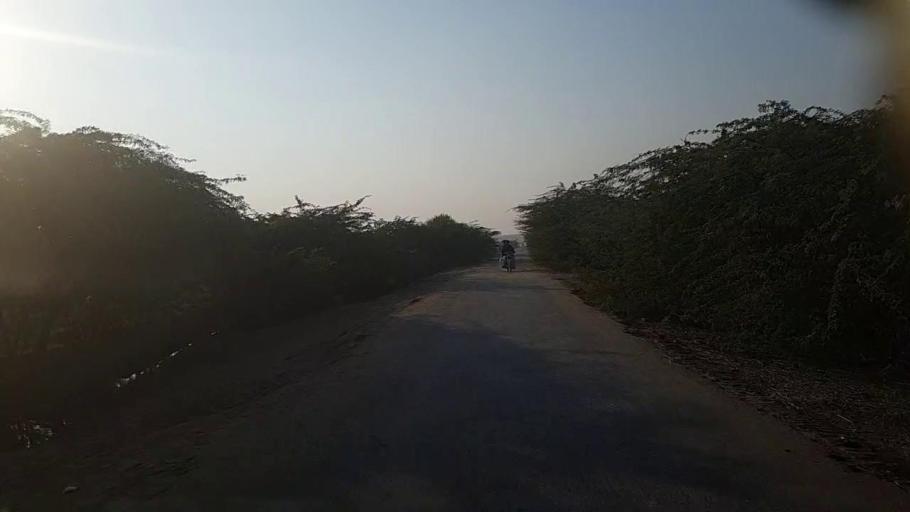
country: PK
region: Sindh
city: Pad Idan
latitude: 26.7217
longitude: 68.4484
